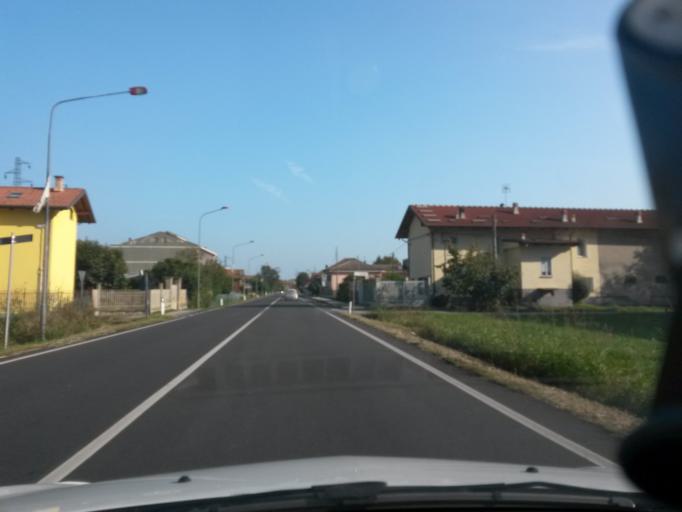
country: IT
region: Piedmont
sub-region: Provincia di Torino
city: Sant'Ambrogio di Torino
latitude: 45.1031
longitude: 7.3542
